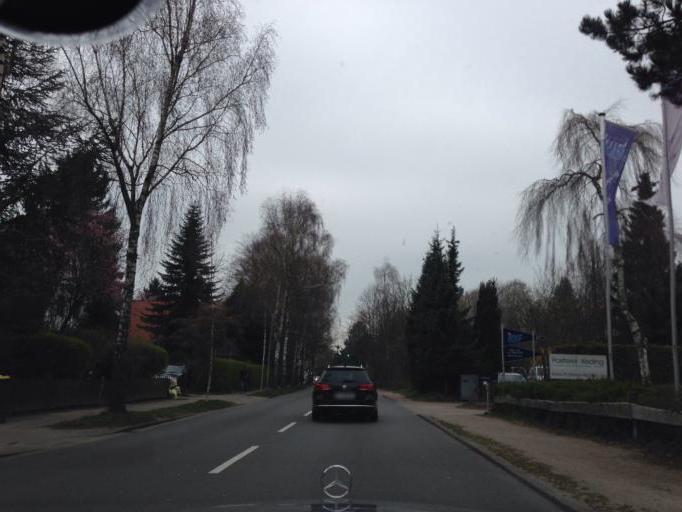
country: DE
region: Hamburg
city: Sasel
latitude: 53.6435
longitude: 10.1252
